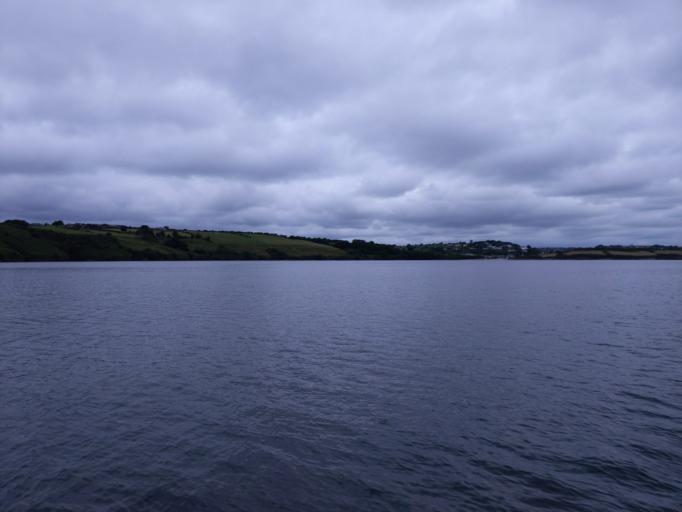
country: IE
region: Munster
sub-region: County Cork
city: Kinsale
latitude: 51.6882
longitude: -8.4988
